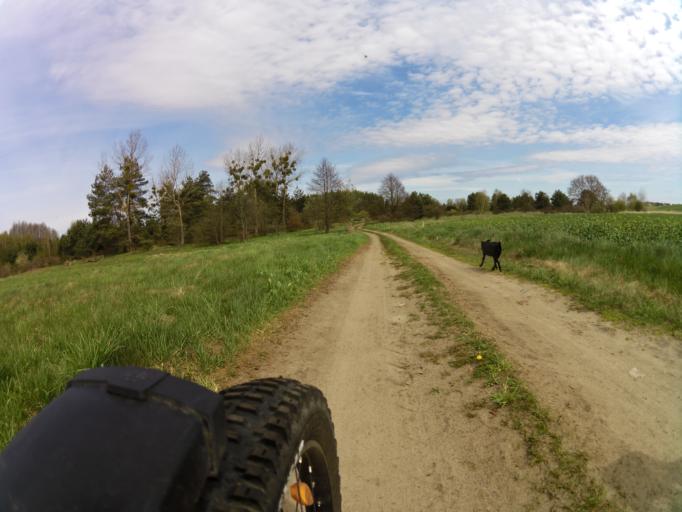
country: PL
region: West Pomeranian Voivodeship
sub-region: Powiat lobeski
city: Resko
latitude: 53.7650
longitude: 15.3815
